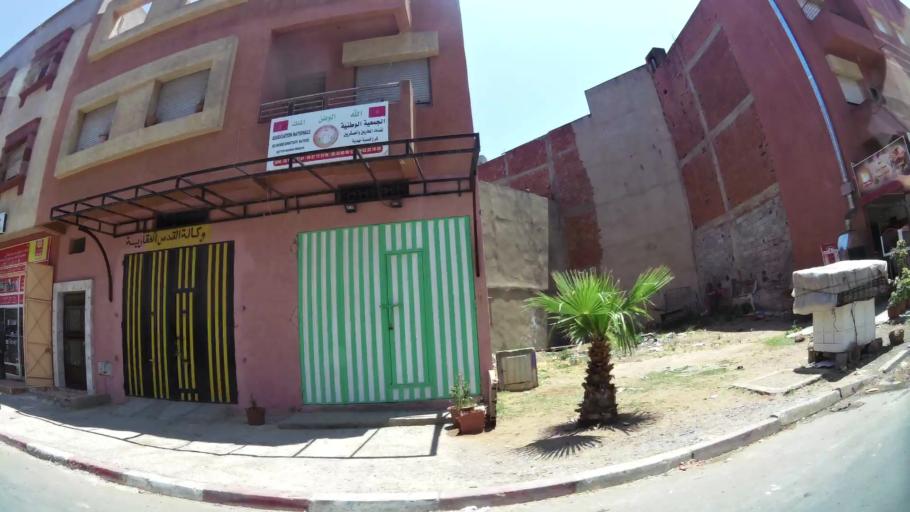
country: MA
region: Gharb-Chrarda-Beni Hssen
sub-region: Kenitra Province
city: Kenitra
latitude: 34.2571
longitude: -6.6497
